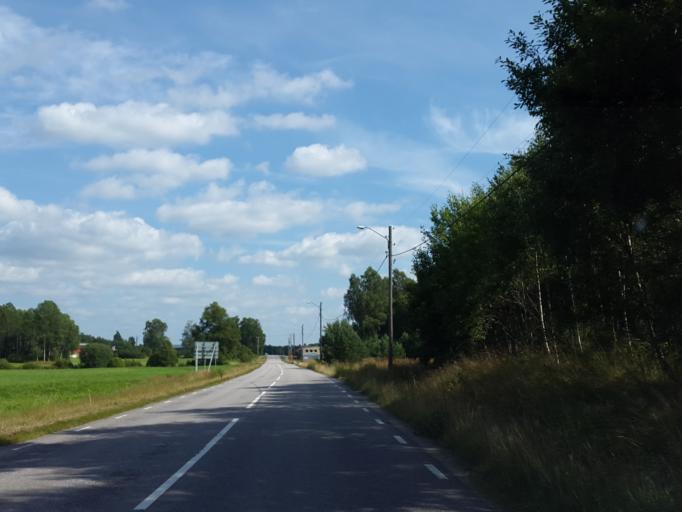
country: SE
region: Vaestra Goetaland
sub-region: Herrljunga Kommun
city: Herrljunga
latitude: 58.0812
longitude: 13.0503
